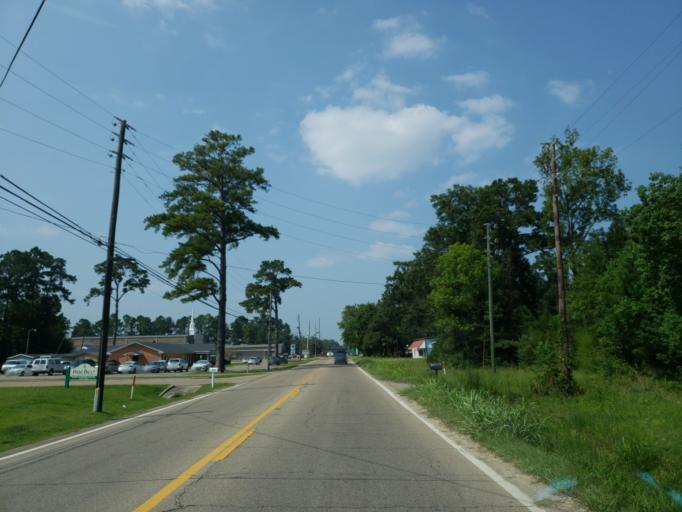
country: US
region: Mississippi
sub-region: Jones County
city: Ellisville
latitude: 31.6298
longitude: -89.1809
